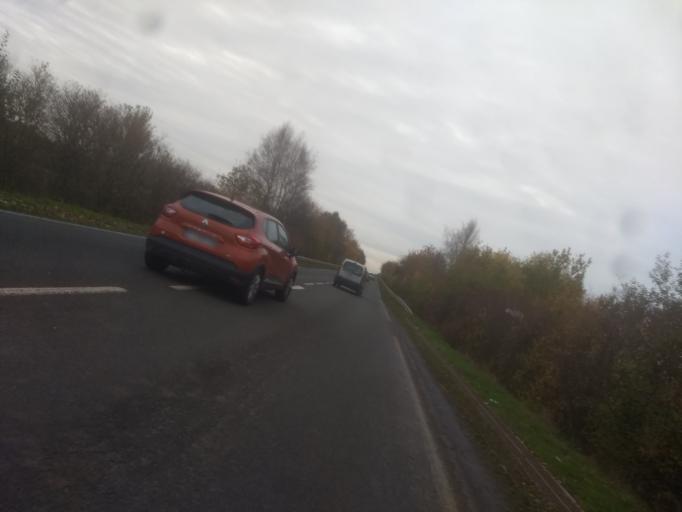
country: FR
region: Nord-Pas-de-Calais
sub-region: Departement du Pas-de-Calais
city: Achicourt
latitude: 50.2768
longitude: 2.7427
